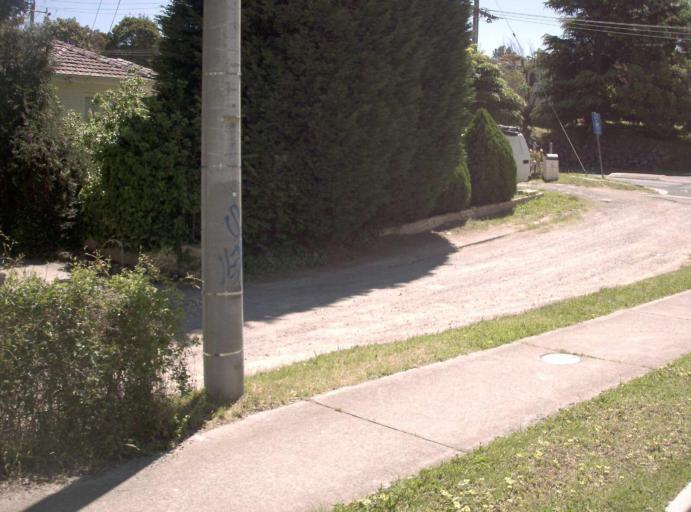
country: AU
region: Victoria
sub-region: Whitehorse
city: Blackburn North
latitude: -37.7987
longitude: 145.1601
